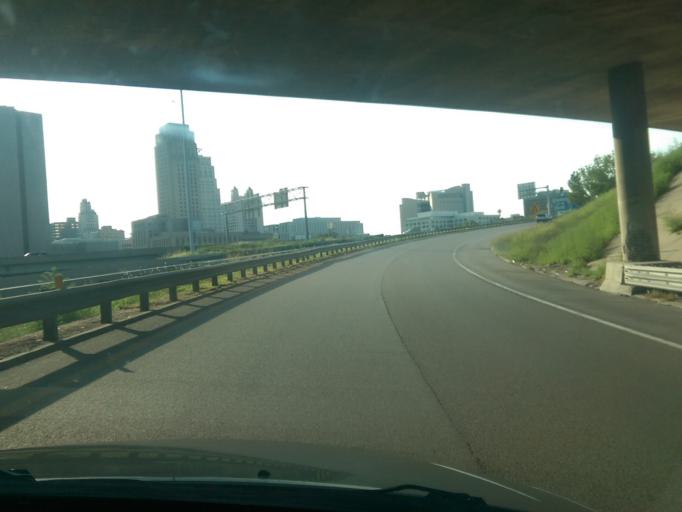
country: US
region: Missouri
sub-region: Jackson County
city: Kansas City
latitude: 39.0978
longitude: -94.5717
